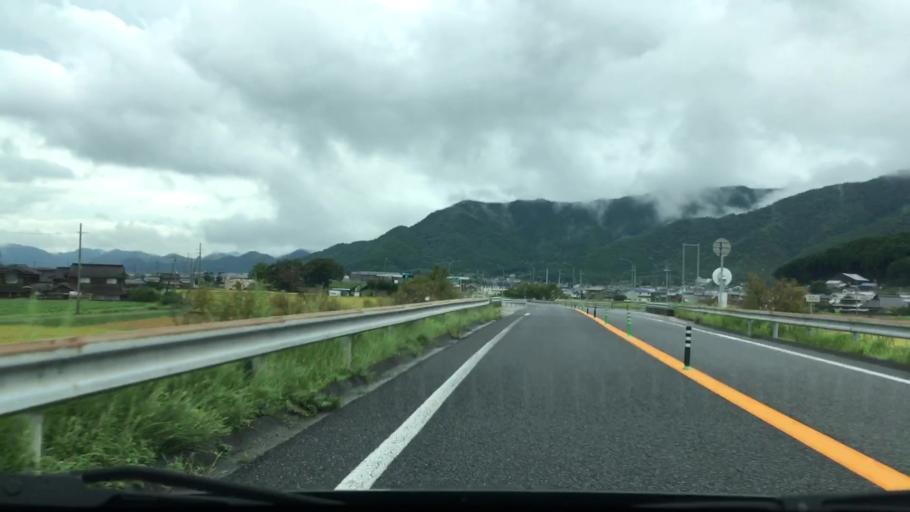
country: JP
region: Hyogo
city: Nishiwaki
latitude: 35.0621
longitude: 134.7663
